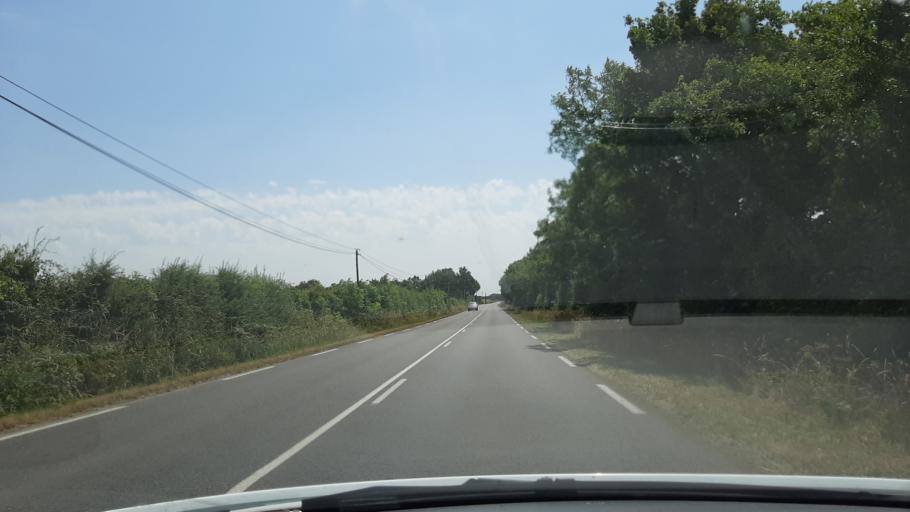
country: FR
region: Pays de la Loire
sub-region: Departement de la Vendee
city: Le Poire-sur-Vie
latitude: 46.7619
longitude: -1.4850
